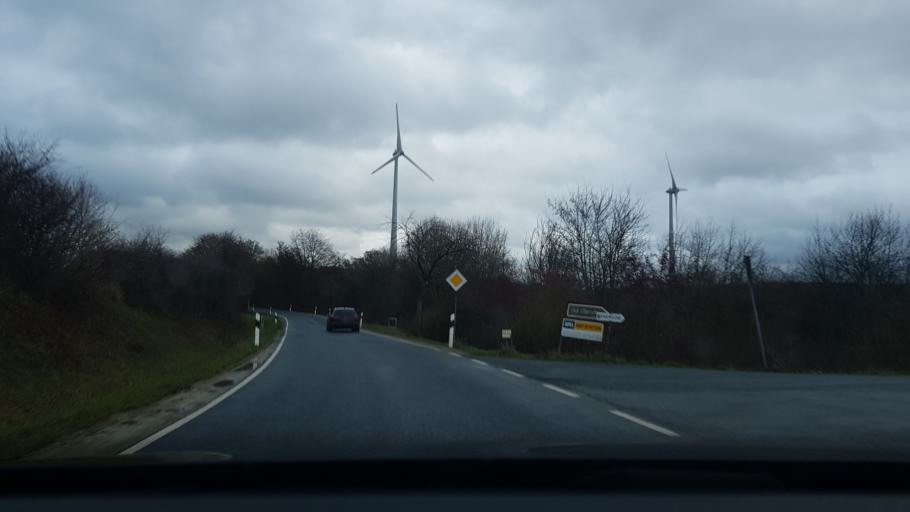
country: DE
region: Lower Saxony
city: Juhnde
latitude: 51.4051
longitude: 9.8084
